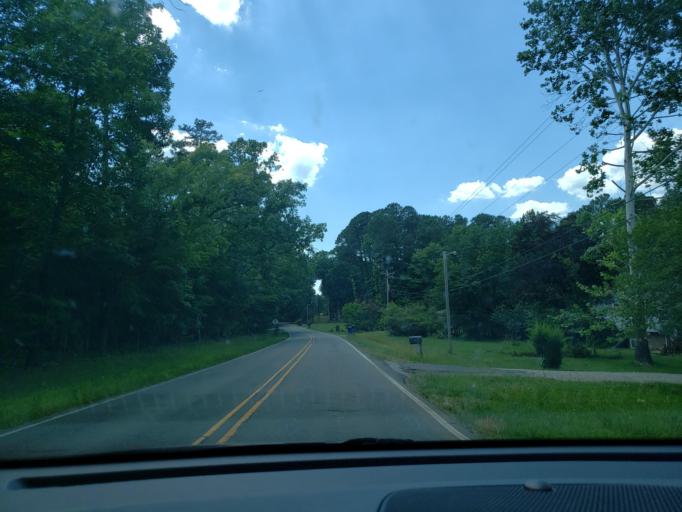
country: US
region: North Carolina
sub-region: Orange County
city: Chapel Hill
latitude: 35.9996
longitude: -79.0188
